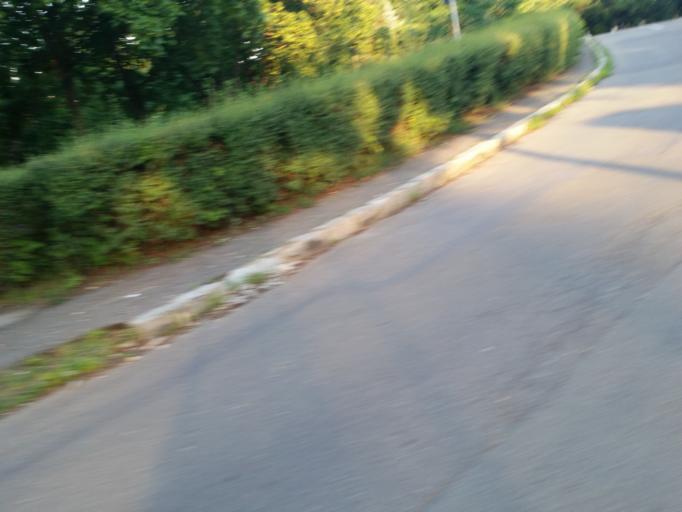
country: RO
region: Cluj
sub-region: Municipiul Cluj-Napoca
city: Cluj-Napoca
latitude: 46.7765
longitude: 23.5816
